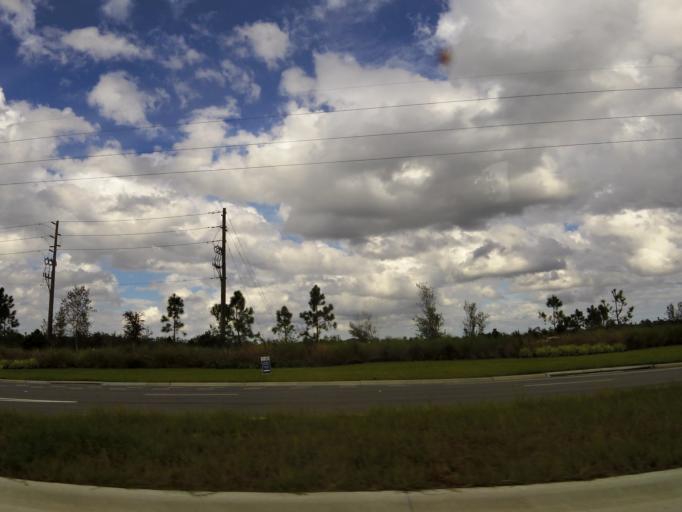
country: US
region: Florida
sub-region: Saint Johns County
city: Villano Beach
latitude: 29.9882
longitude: -81.4507
